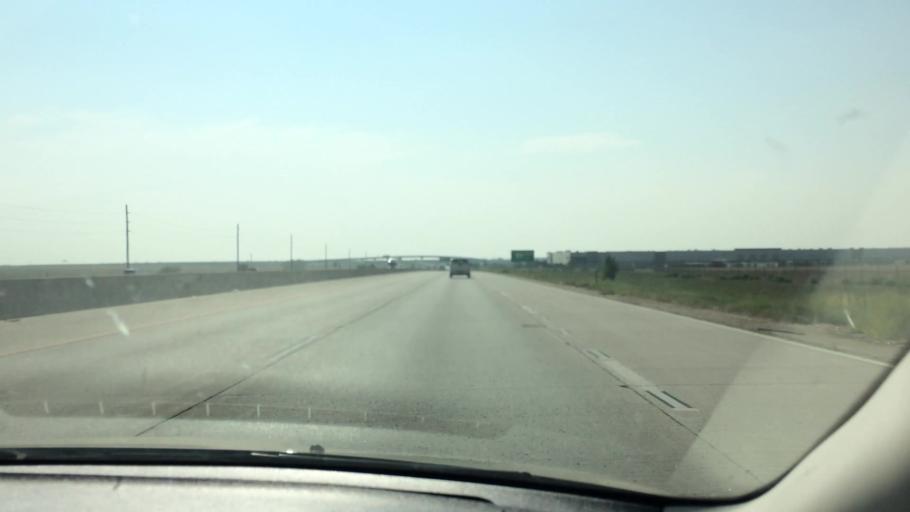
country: US
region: Colorado
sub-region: Adams County
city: Aurora
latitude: 39.7404
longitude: -104.6975
